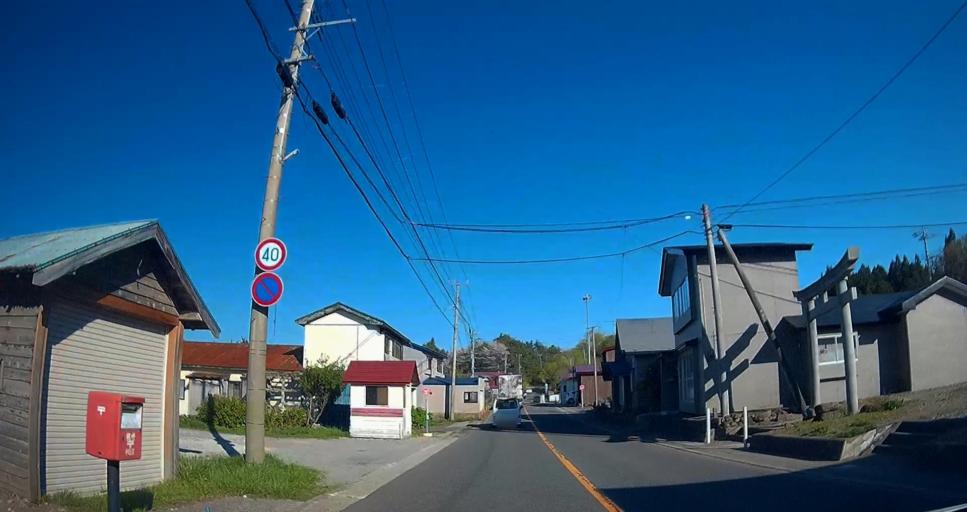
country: JP
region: Aomori
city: Mutsu
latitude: 41.4550
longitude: 141.1162
